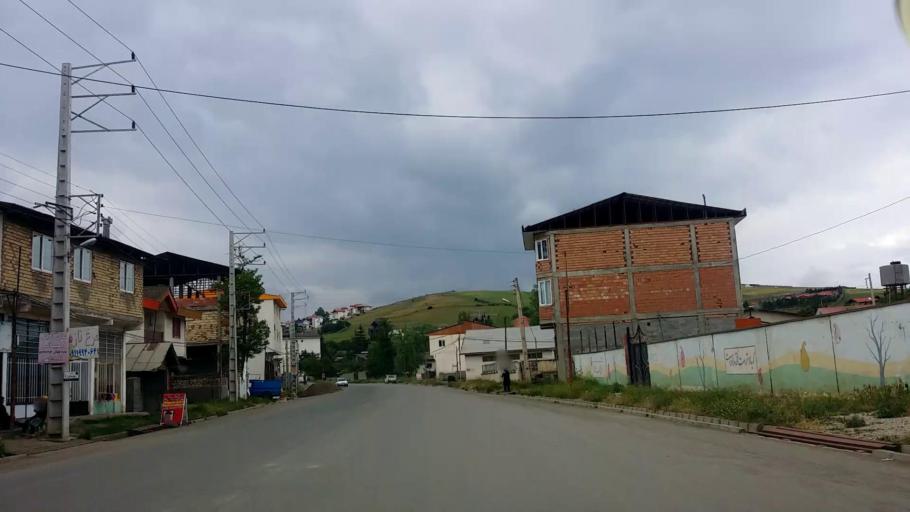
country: IR
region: Mazandaran
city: Chalus
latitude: 36.5128
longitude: 51.2520
